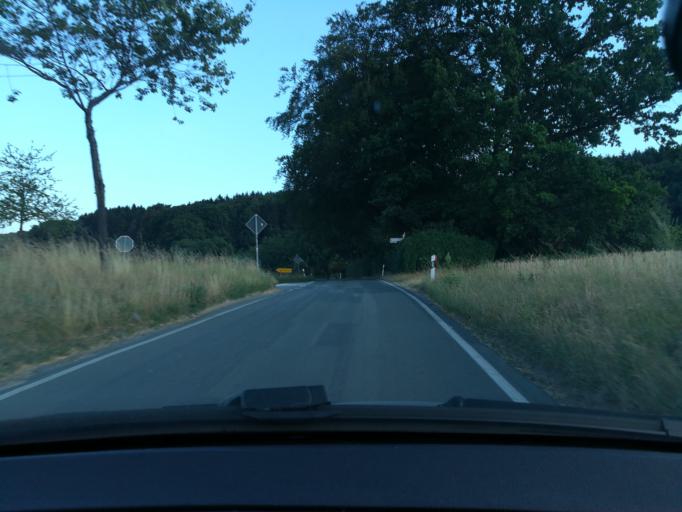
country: DE
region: Lower Saxony
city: Hagen
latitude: 52.1717
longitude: 7.9552
